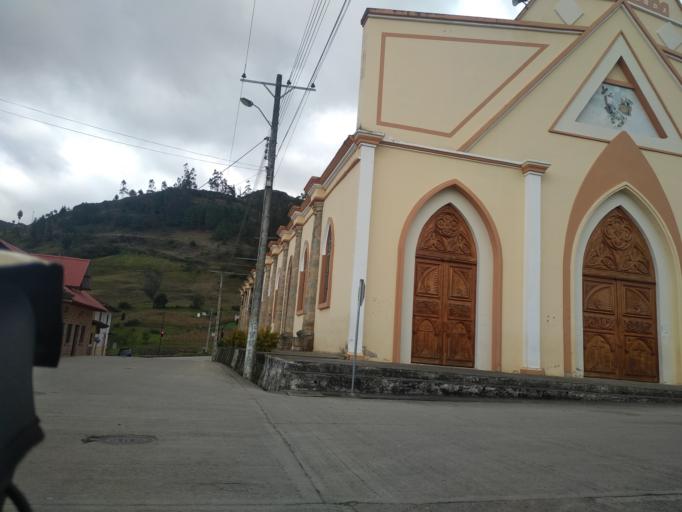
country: EC
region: Loja
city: Loja
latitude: -3.6041
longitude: -79.2114
